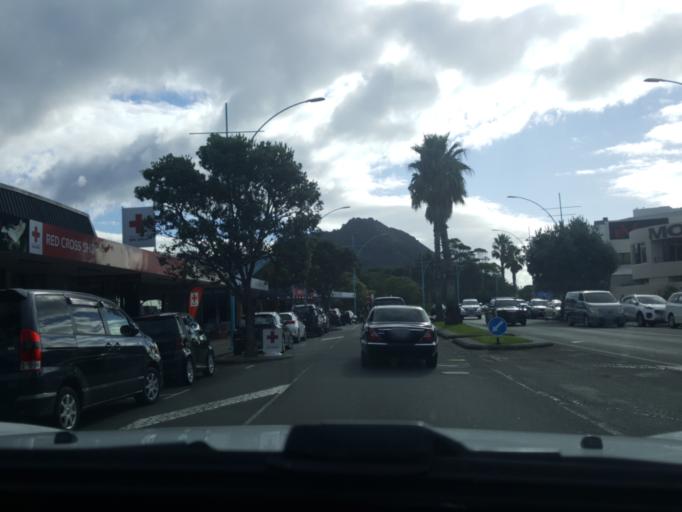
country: NZ
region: Bay of Plenty
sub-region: Tauranga City
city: Tauranga
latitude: -37.6418
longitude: 176.1853
